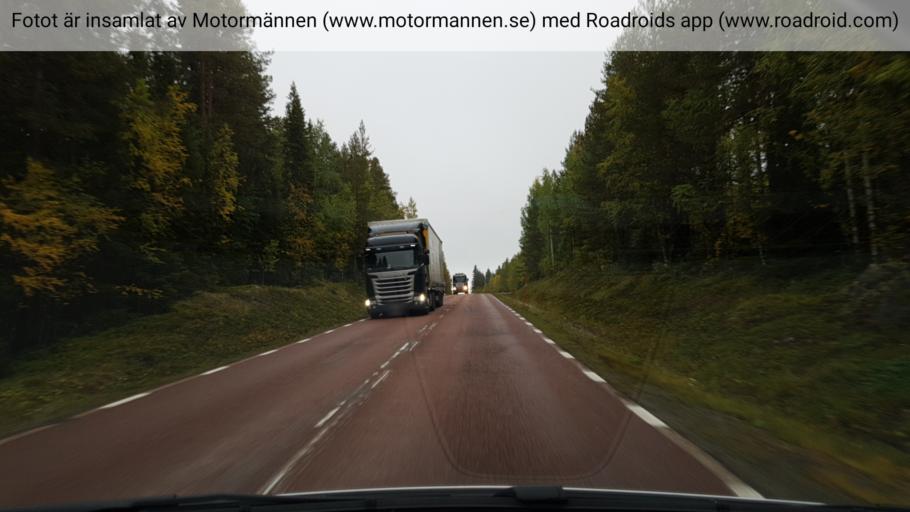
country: SE
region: Vaesterbotten
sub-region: Dorotea Kommun
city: Dorotea
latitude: 64.0972
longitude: 16.0865
